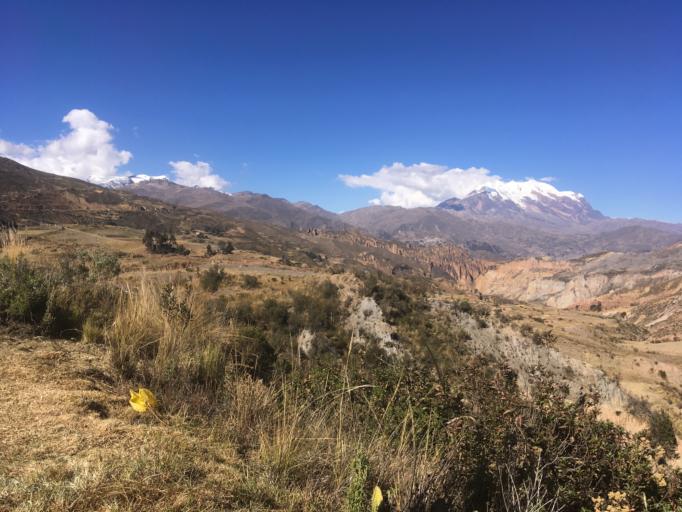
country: BO
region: La Paz
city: La Paz
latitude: -16.5492
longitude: -68.0071
